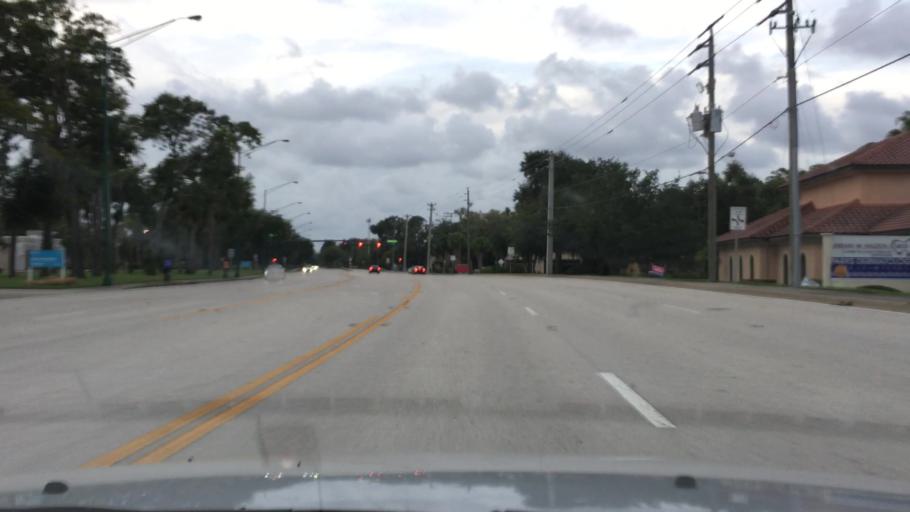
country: US
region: Florida
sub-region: Volusia County
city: Ormond Beach
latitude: 29.2843
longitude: -81.0828
